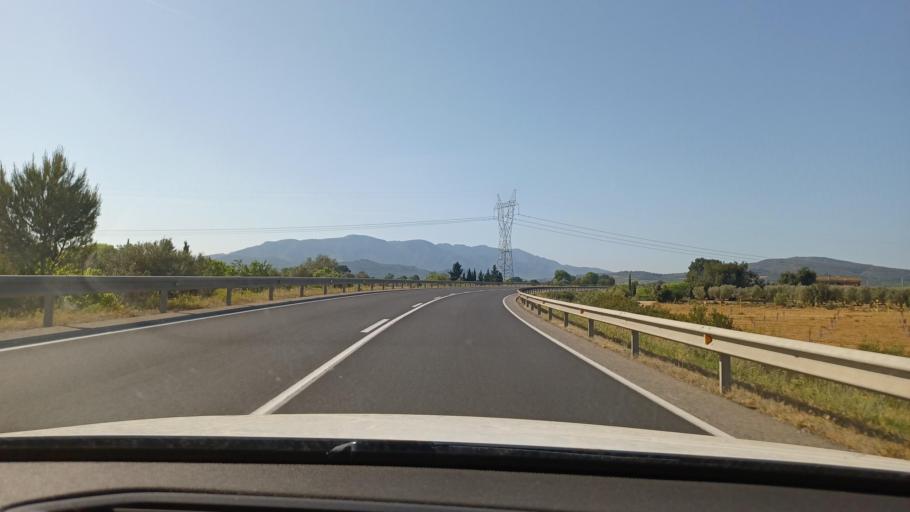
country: ES
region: Catalonia
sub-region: Provincia de Tarragona
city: Santa Barbara
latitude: 40.7122
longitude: 0.5068
